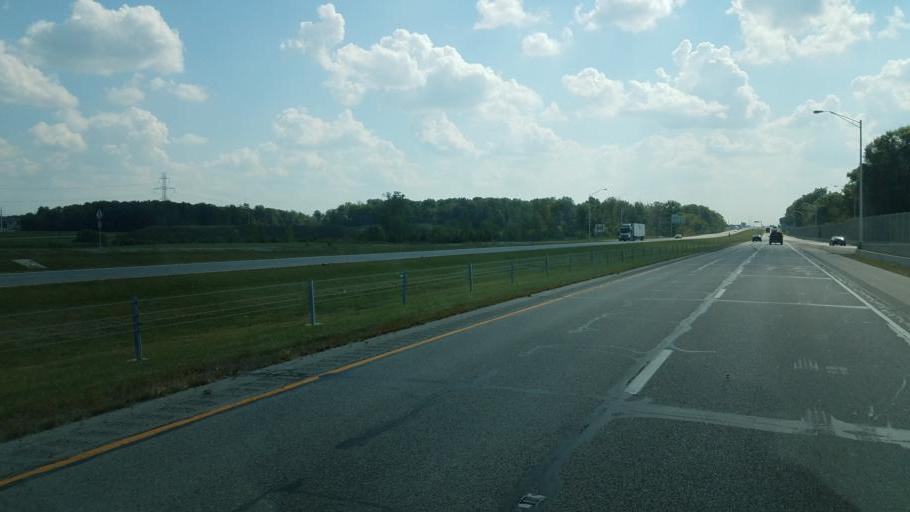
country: US
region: Indiana
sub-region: Allen County
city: Fort Wayne
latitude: 41.1983
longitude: -85.1043
